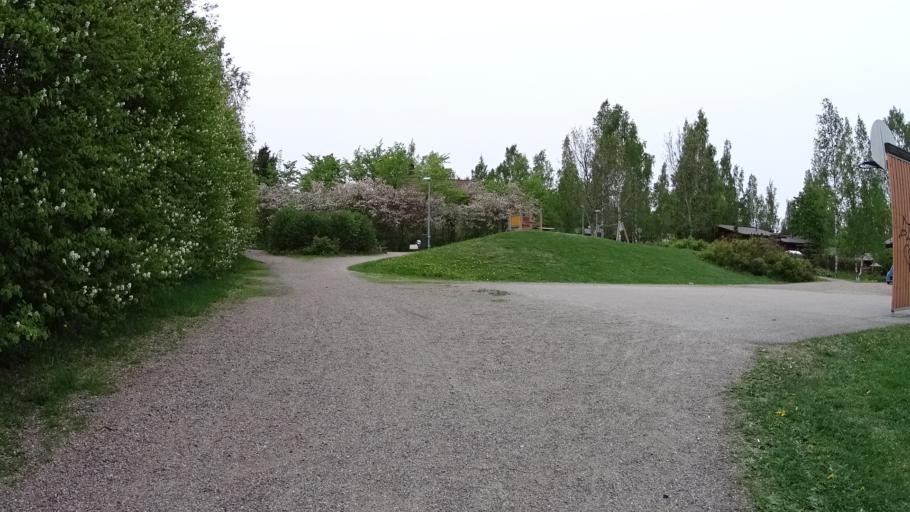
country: FI
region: Uusimaa
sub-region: Helsinki
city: Kilo
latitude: 60.2662
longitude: 24.7940
